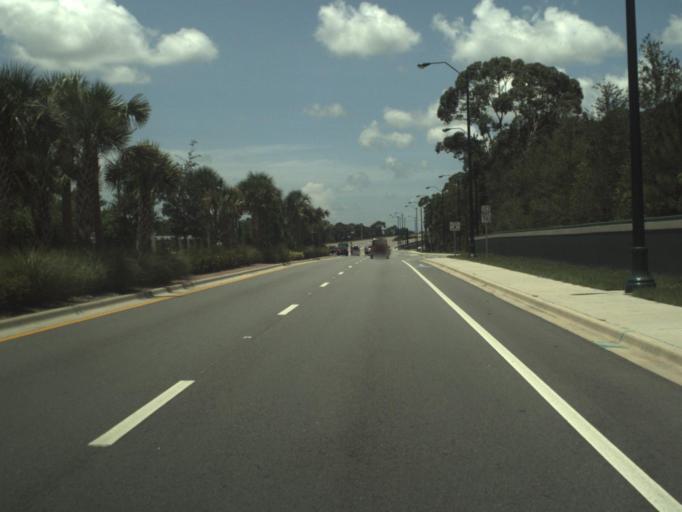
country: US
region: Florida
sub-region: Martin County
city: Palm City
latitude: 27.1595
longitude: -80.2440
